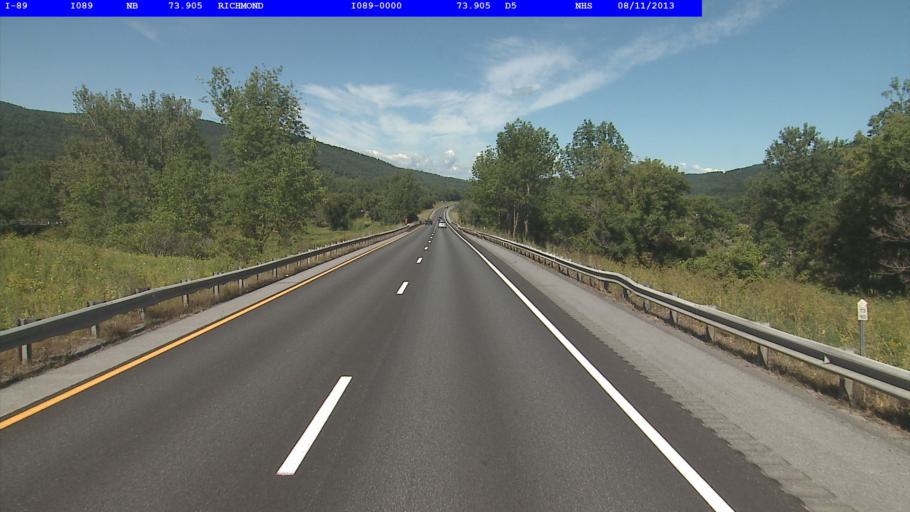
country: US
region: Vermont
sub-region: Chittenden County
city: Jericho
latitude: 44.3885
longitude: -72.9408
